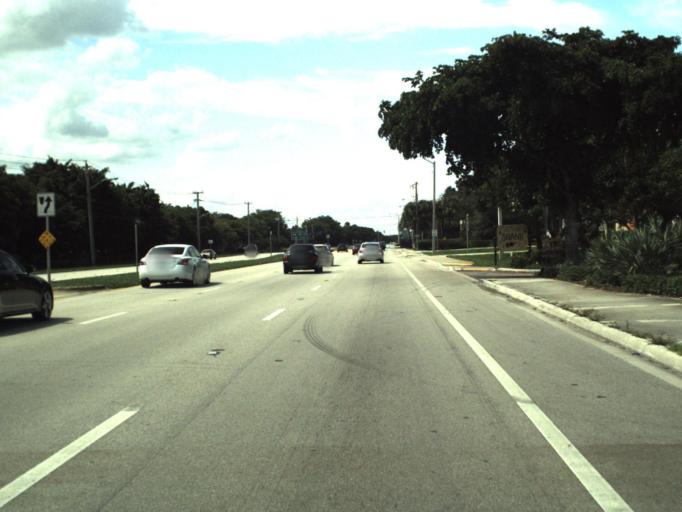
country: US
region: Florida
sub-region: Broward County
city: Davie
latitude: 26.0692
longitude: -80.2523
